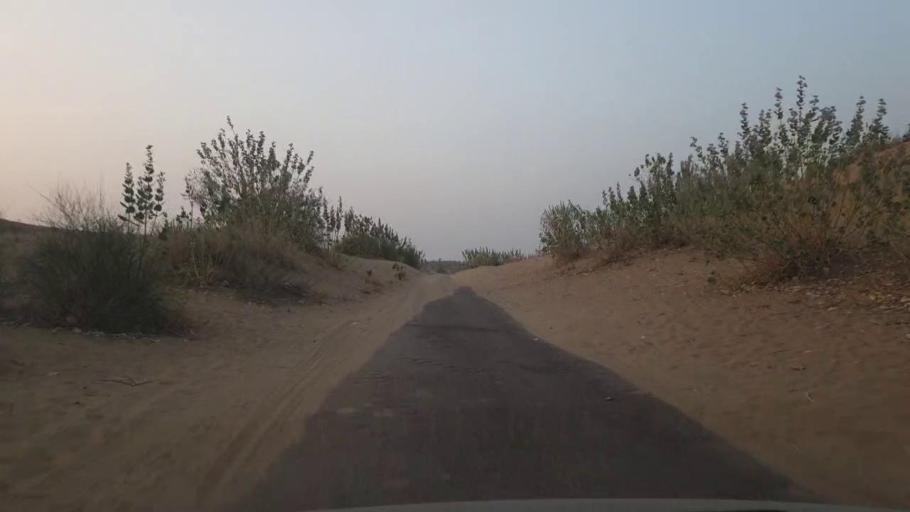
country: PK
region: Sindh
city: Umarkot
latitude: 25.3134
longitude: 70.0600
